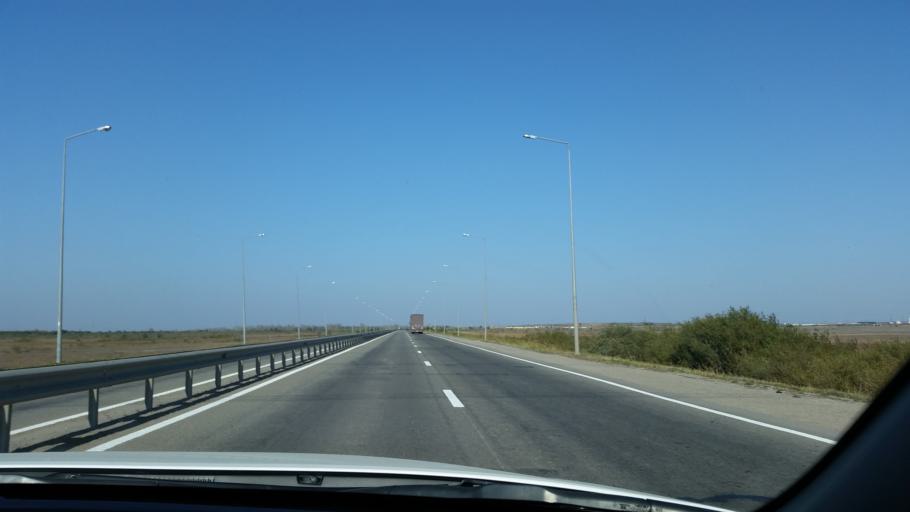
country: KZ
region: Astana Qalasy
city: Astana
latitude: 51.2379
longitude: 71.3321
